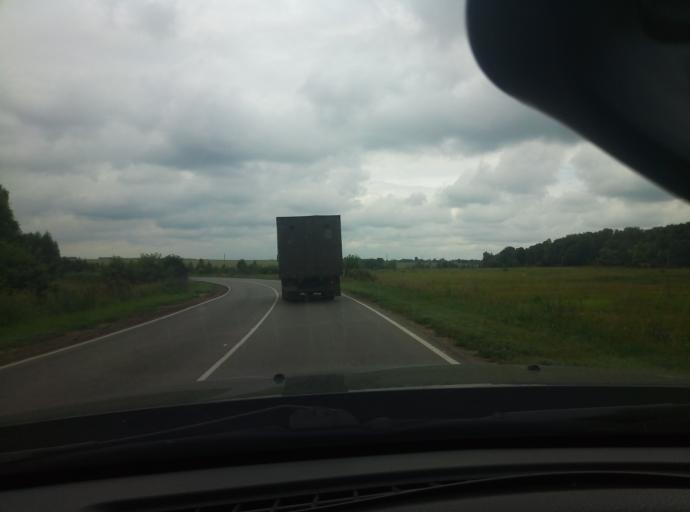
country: RU
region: Tula
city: Kimovsk
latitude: 53.9513
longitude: 38.5362
